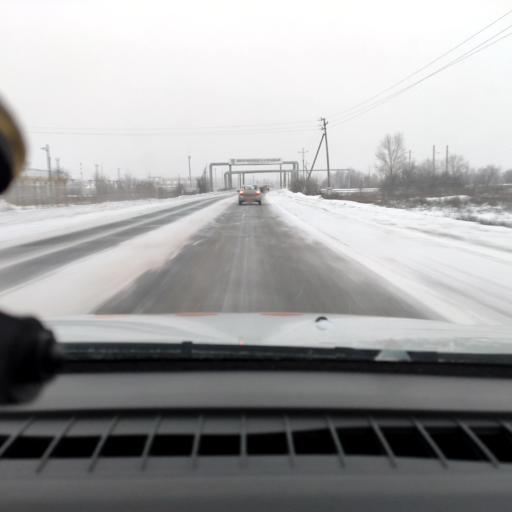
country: RU
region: Samara
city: Otradnyy
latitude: 53.3464
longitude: 51.3067
